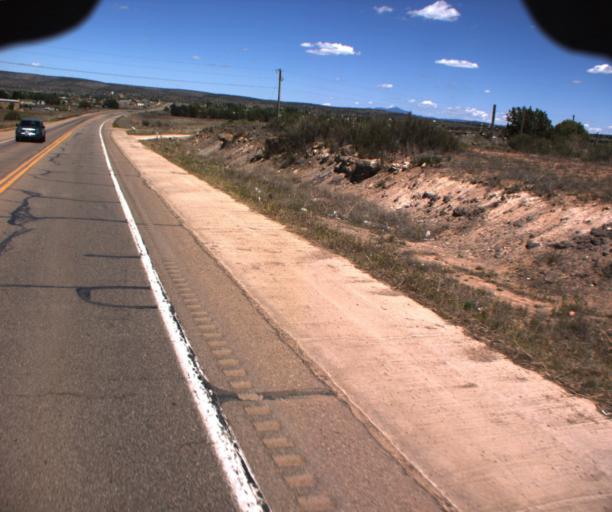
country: US
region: Arizona
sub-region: Yavapai County
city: Paulden
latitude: 34.8912
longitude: -112.4673
